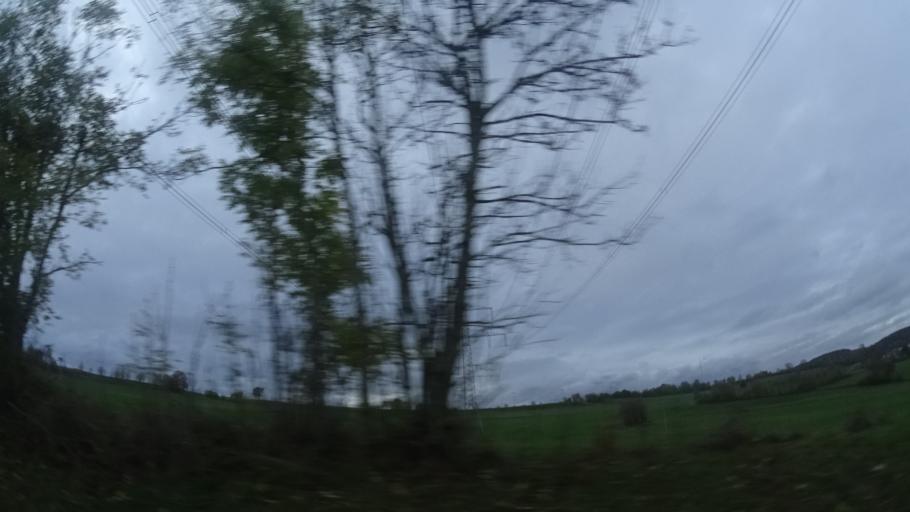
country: DE
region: Hesse
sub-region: Regierungsbezirk Giessen
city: Freiensteinau
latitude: 50.3883
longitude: 9.4329
